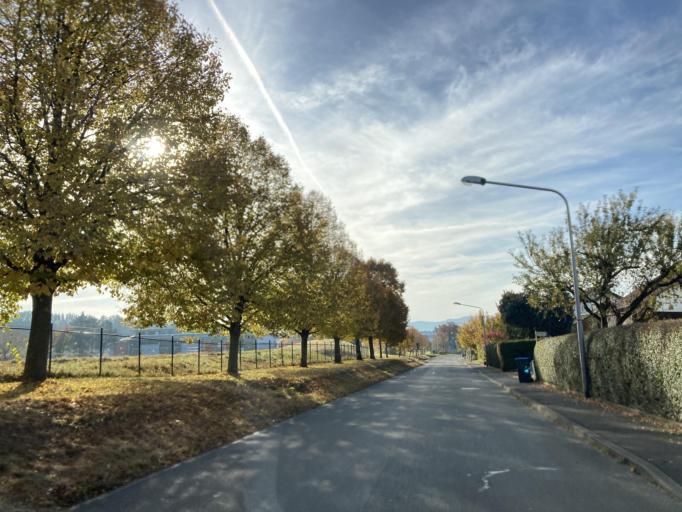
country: DE
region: Baden-Wuerttemberg
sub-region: Tuebingen Region
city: Bodelshausen
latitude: 48.4003
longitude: 8.9762
